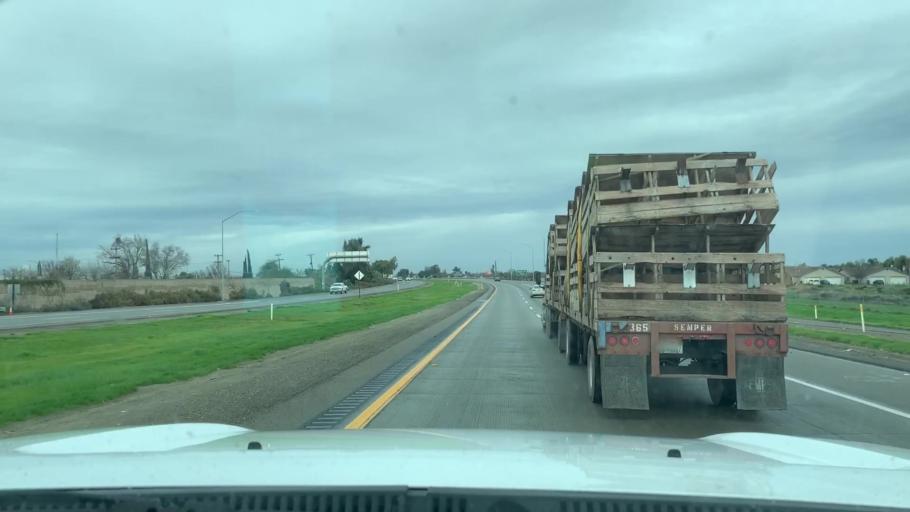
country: US
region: California
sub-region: Kings County
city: Lemoore
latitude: 36.2853
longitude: -119.8077
